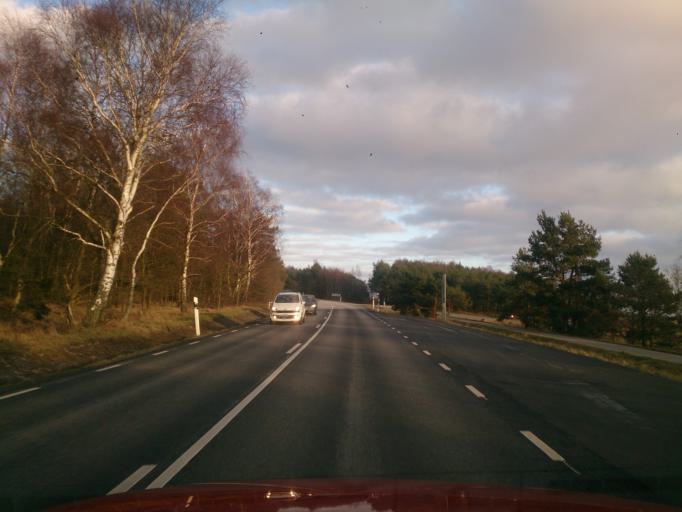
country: SE
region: Skane
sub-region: Ystads Kommun
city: Ystad
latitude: 55.4264
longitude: 13.7645
